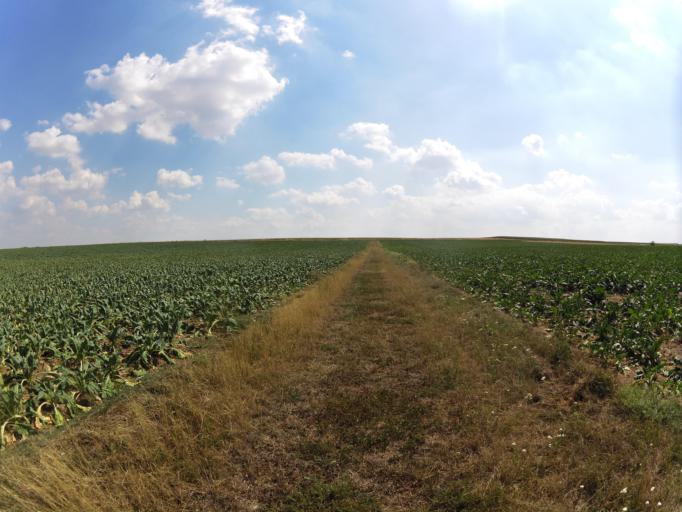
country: DE
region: Bavaria
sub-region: Regierungsbezirk Unterfranken
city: Ochsenfurt
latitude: 49.6393
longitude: 10.0592
